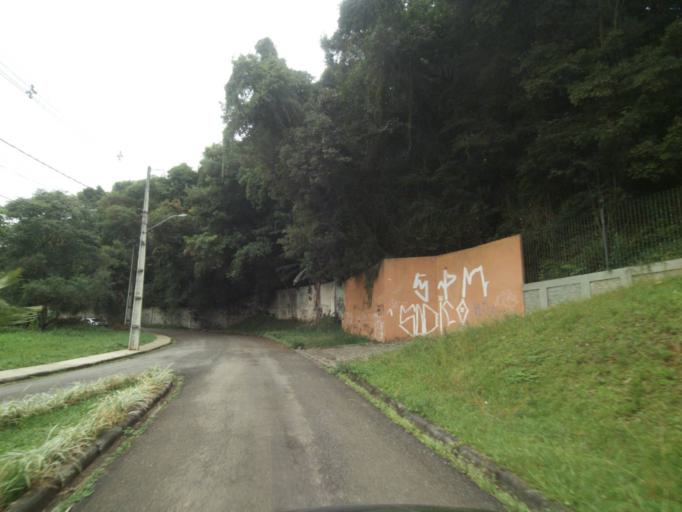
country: BR
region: Parana
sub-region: Curitiba
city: Curitiba
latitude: -25.4648
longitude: -49.3227
